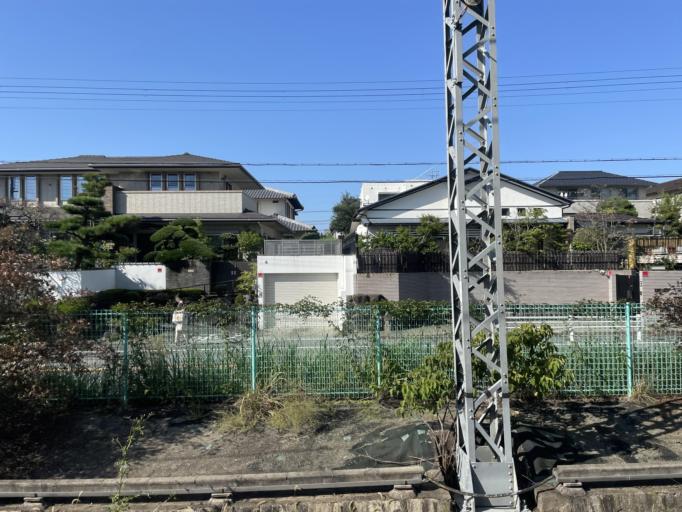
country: JP
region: Nara
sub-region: Ikoma-shi
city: Ikoma
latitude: 34.6965
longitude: 135.7457
